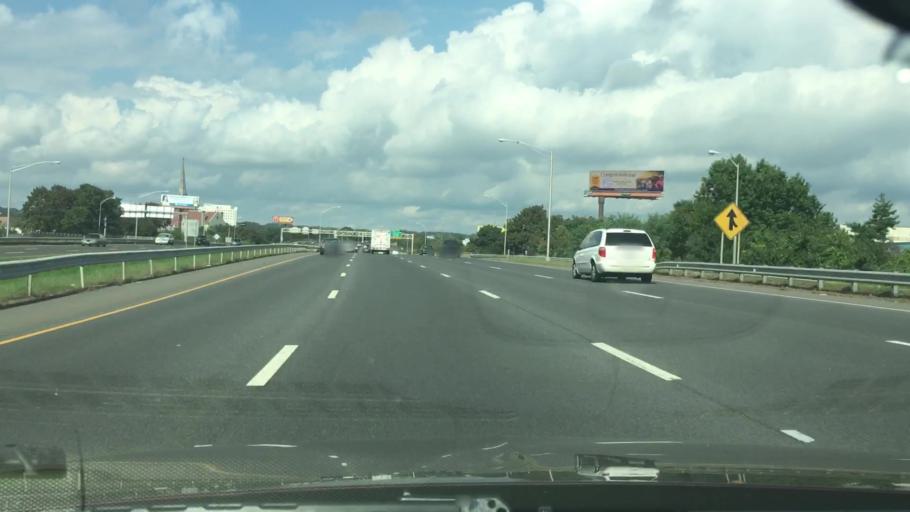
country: US
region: Connecticut
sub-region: Fairfield County
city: Bridgeport
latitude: 41.1885
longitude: -73.1930
